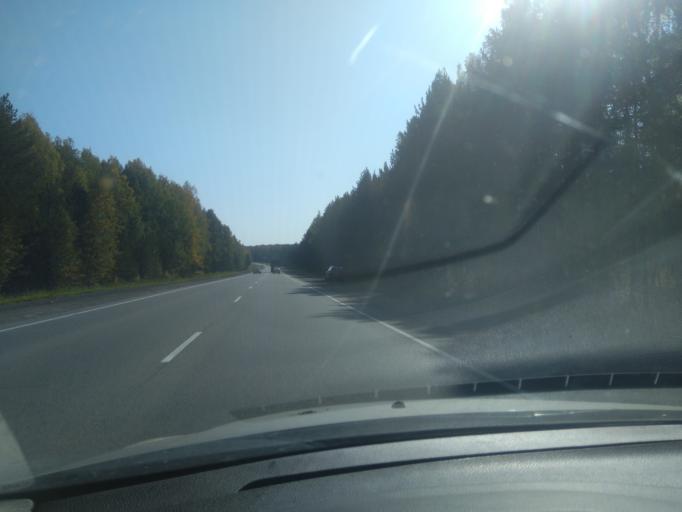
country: RU
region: Sverdlovsk
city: Verkhneye Dubrovo
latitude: 56.7110
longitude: 61.0641
